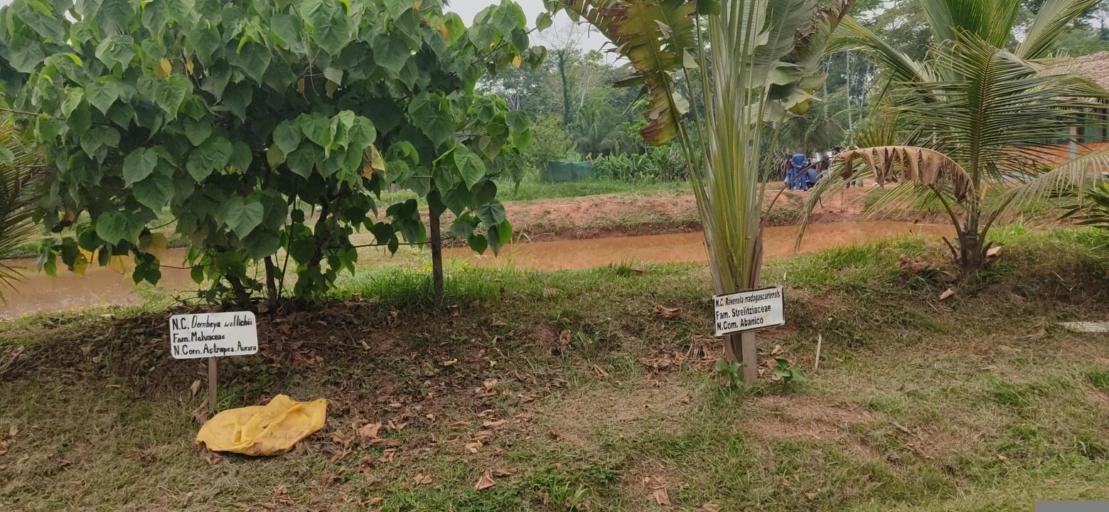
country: BO
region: La Paz
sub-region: Provincia Larecaja
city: Guanay
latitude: -15.5655
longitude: -67.3244
